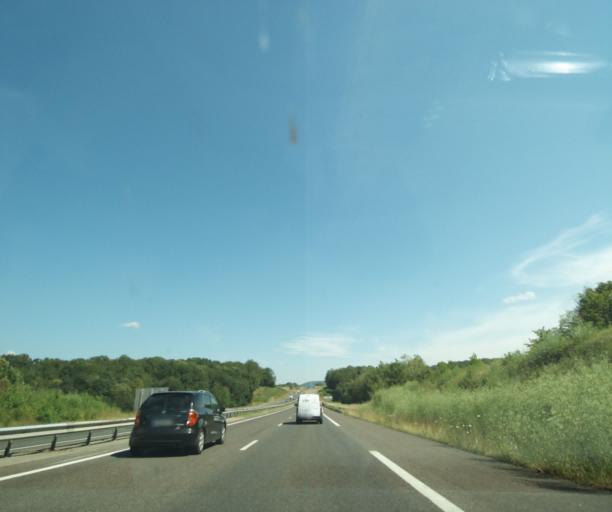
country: FR
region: Lorraine
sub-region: Departement de Meurthe-et-Moselle
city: Dommartin-les-Toul
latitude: 48.6442
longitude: 5.8804
